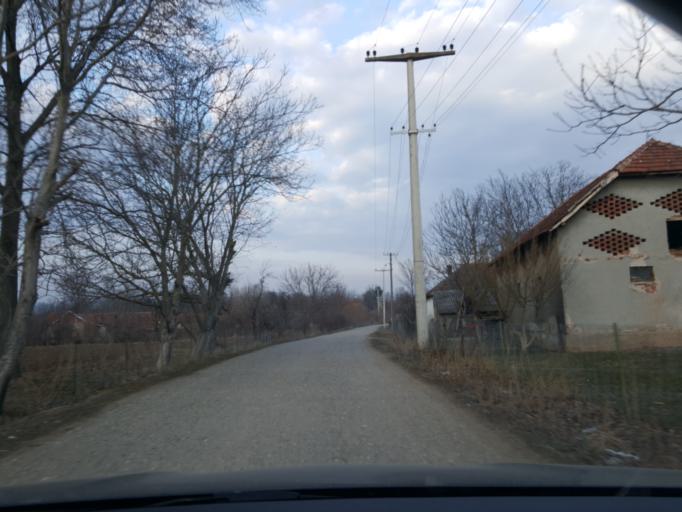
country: RS
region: Central Serbia
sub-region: Nisavski Okrug
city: Aleksinac
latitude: 43.5925
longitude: 21.6200
